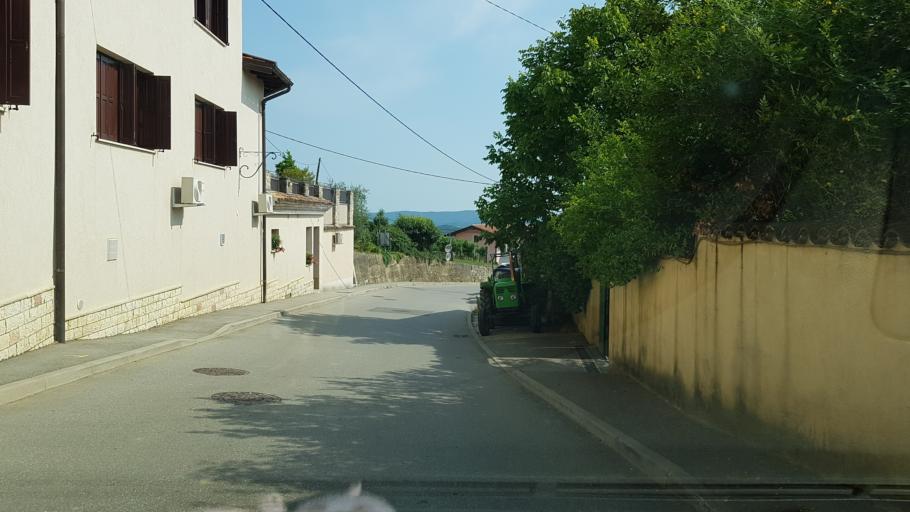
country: SI
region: Brda
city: Dobrovo
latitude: 45.9847
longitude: 13.5213
